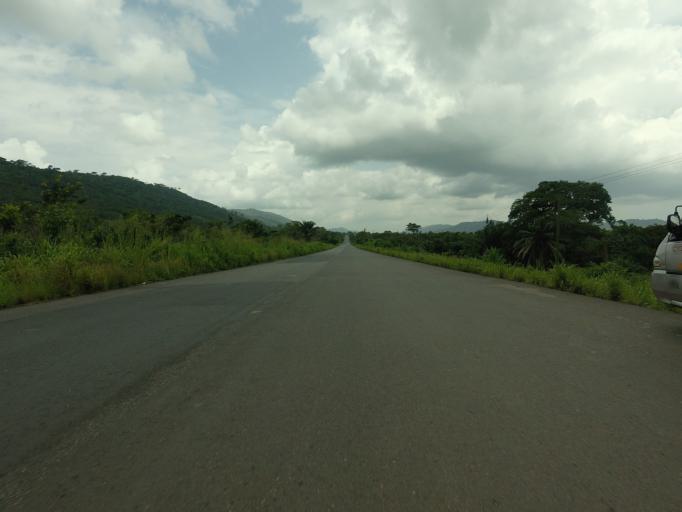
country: GH
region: Volta
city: Ho
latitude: 6.6169
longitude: 0.3044
